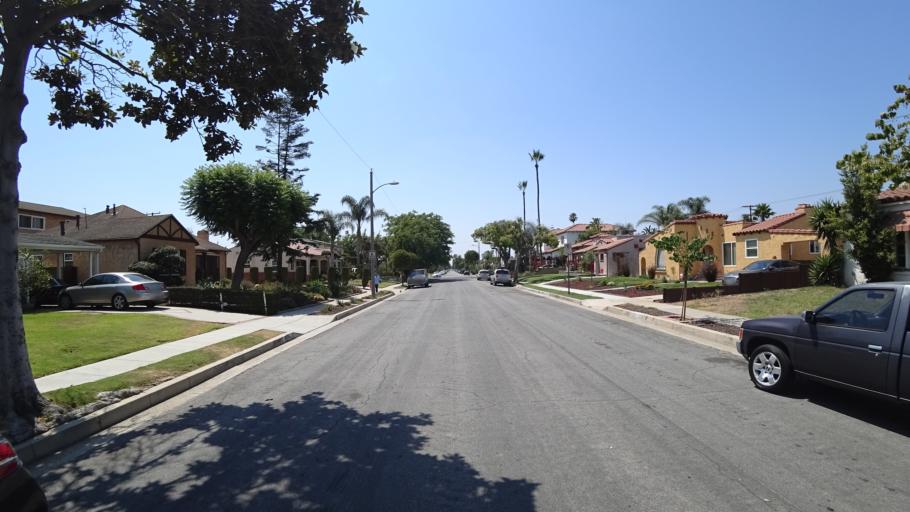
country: US
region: California
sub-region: Los Angeles County
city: Westmont
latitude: 33.9587
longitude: -118.3210
